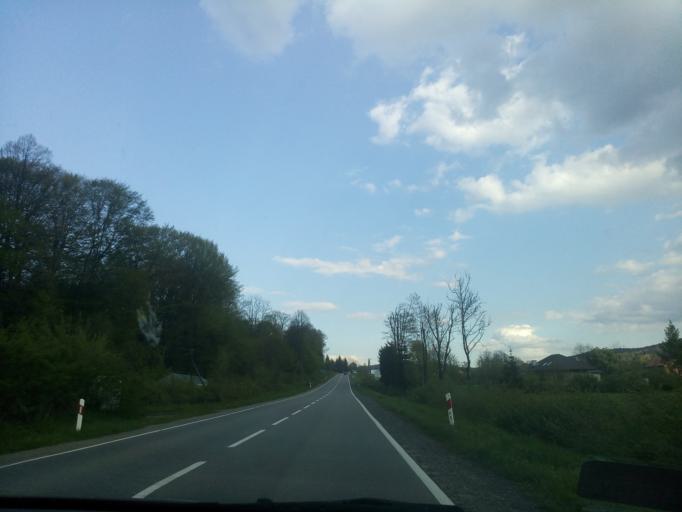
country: PL
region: Lesser Poland Voivodeship
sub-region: Powiat nowosadecki
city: Labowa
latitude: 49.5330
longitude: 20.8440
